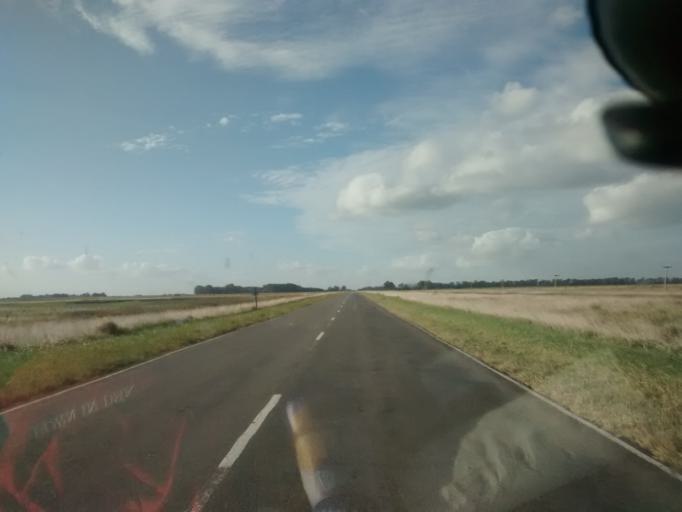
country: AR
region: Buenos Aires
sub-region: Partido de Ayacucho
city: Ayacucho
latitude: -36.6796
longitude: -58.5749
